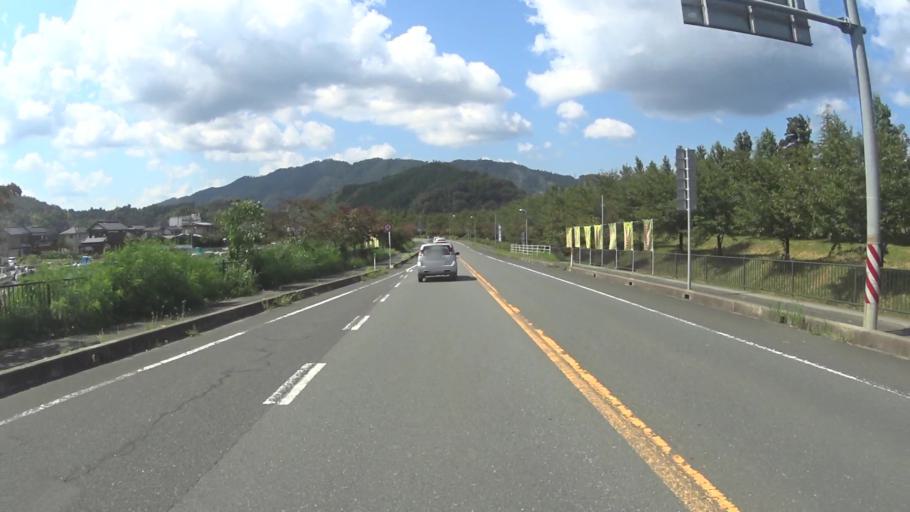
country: JP
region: Kyoto
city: Miyazu
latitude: 35.5526
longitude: 135.1571
